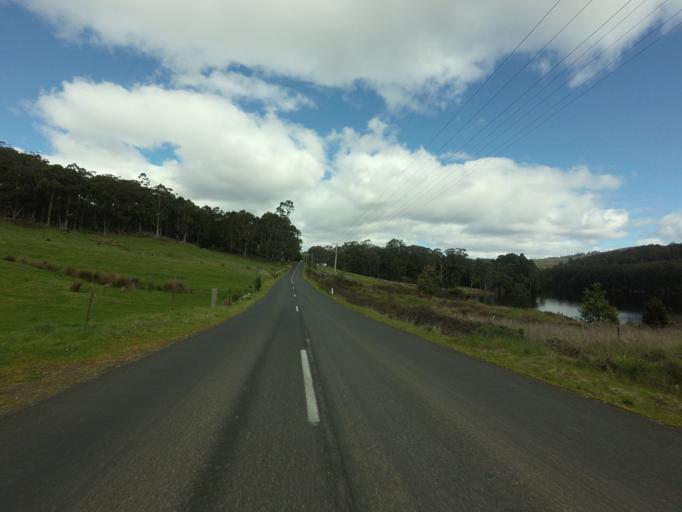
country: AU
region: Tasmania
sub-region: Huon Valley
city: Geeveston
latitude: -43.1873
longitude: 146.9336
